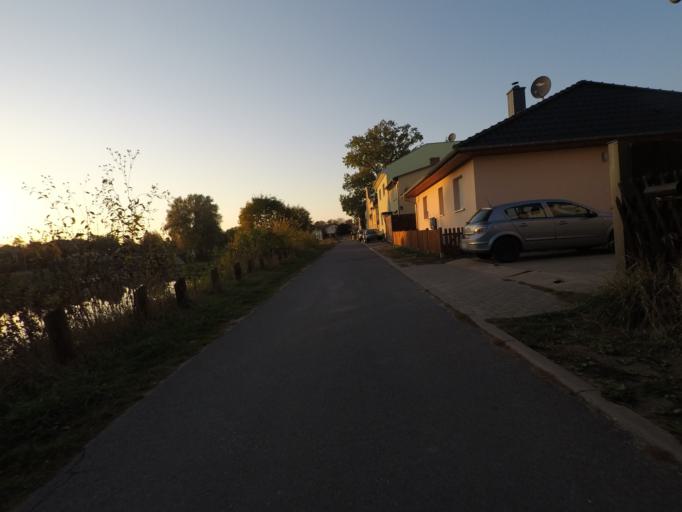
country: DE
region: Brandenburg
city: Melchow
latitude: 52.8465
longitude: 13.6857
